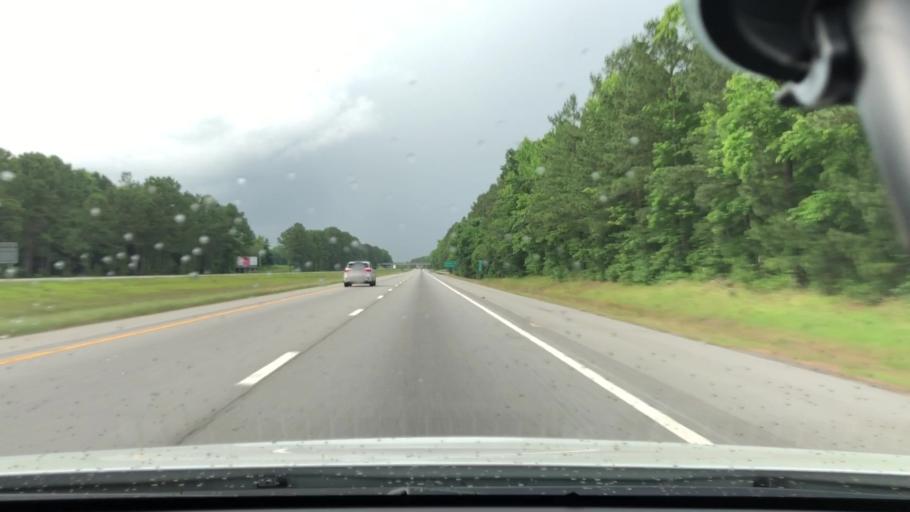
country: US
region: North Carolina
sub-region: Halifax County
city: Enfield
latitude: 36.2838
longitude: -77.7169
